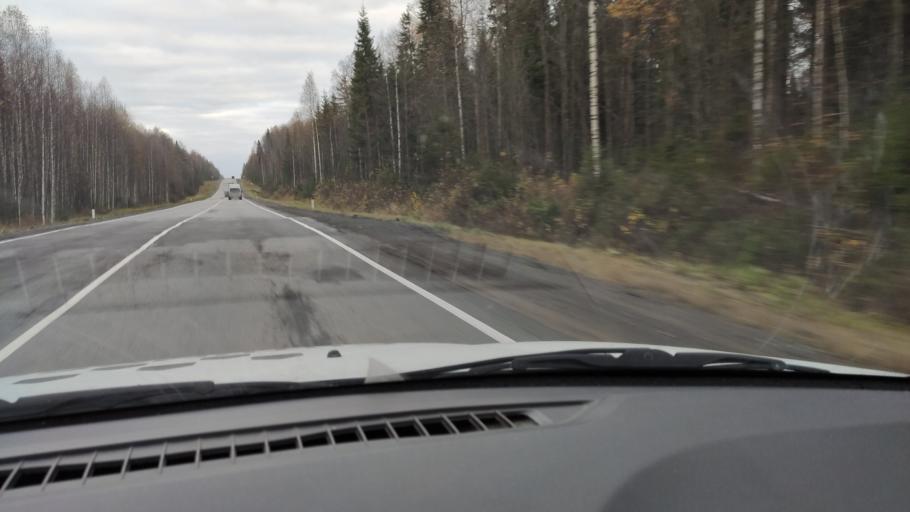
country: RU
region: Kirov
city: Chernaya Kholunitsa
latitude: 58.8587
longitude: 51.6303
